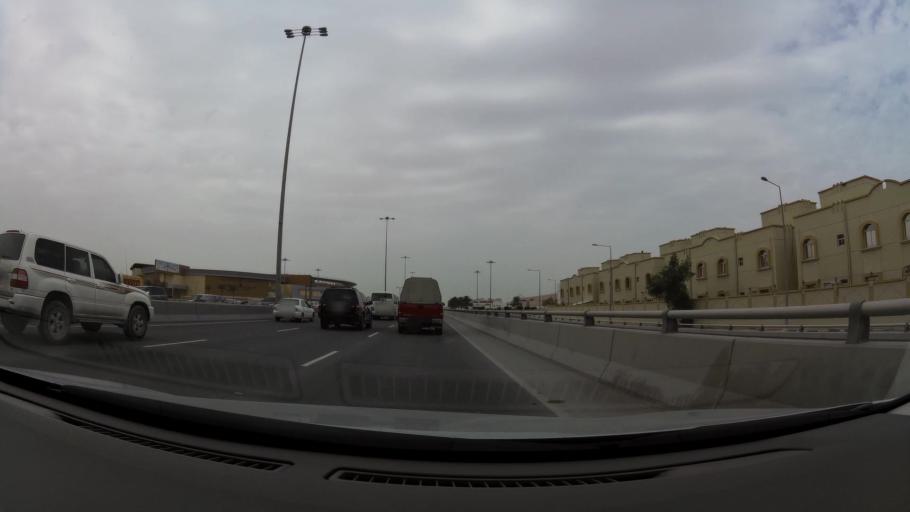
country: QA
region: Baladiyat ar Rayyan
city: Ar Rayyan
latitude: 25.3305
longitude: 51.4652
